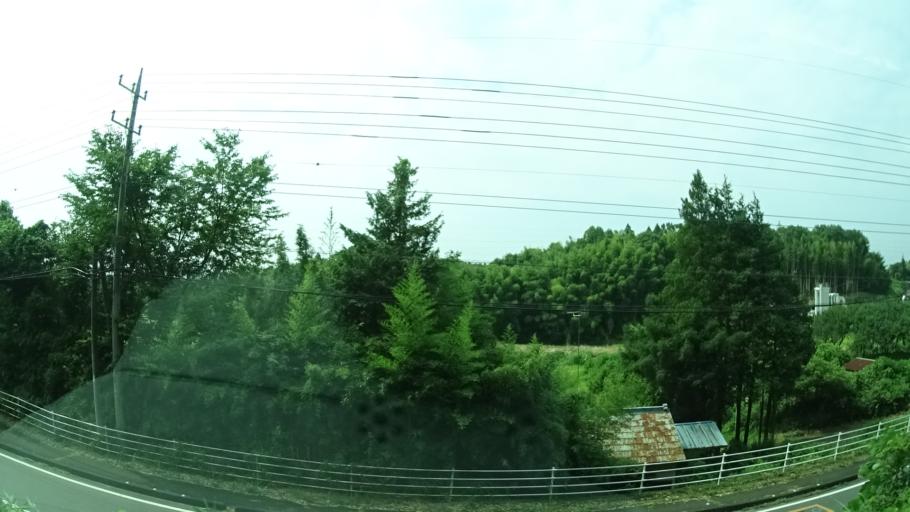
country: JP
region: Tochigi
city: Mashiko
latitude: 36.5234
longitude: 140.0933
